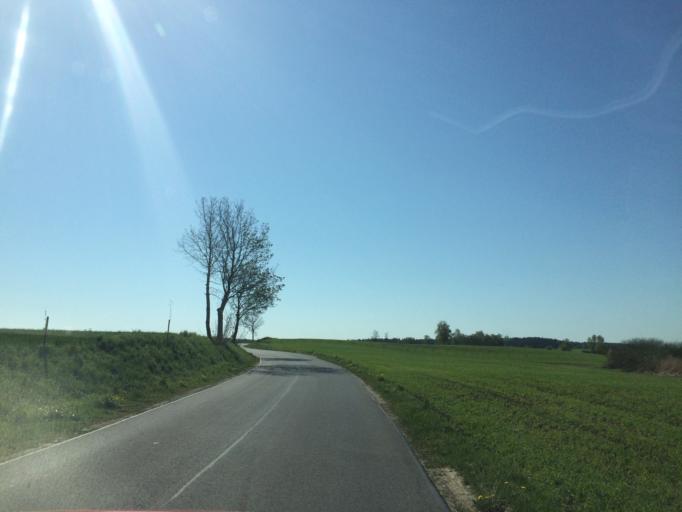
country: PL
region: Warmian-Masurian Voivodeship
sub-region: Powiat nowomiejski
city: Nowe Miasto Lubawskie
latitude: 53.5058
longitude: 19.5734
